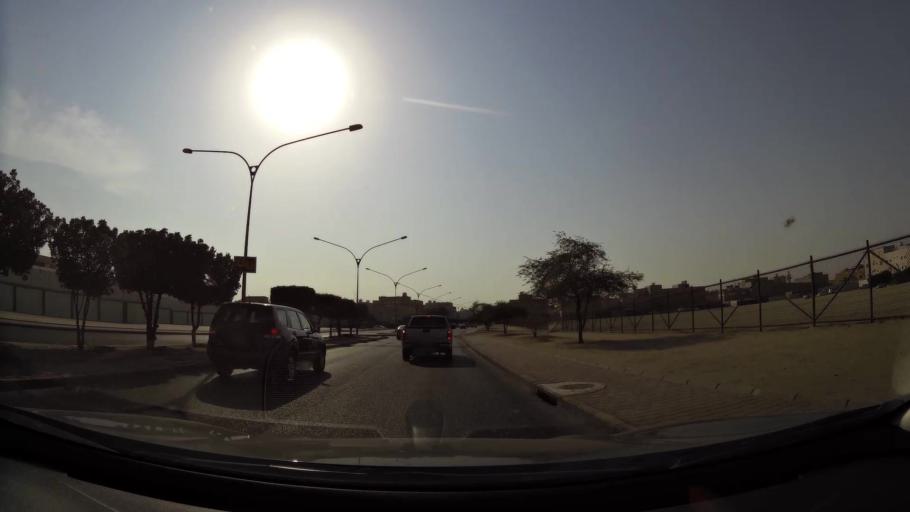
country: KW
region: Mubarak al Kabir
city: Mubarak al Kabir
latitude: 29.1637
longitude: 48.0665
